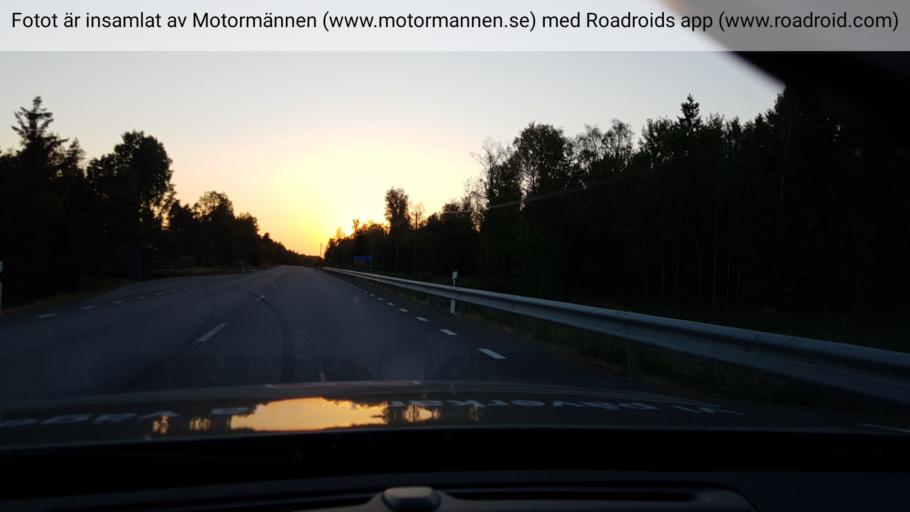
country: SE
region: Uppsala
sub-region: Osthammars Kommun
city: Bjorklinge
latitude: 59.9691
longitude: 17.3738
